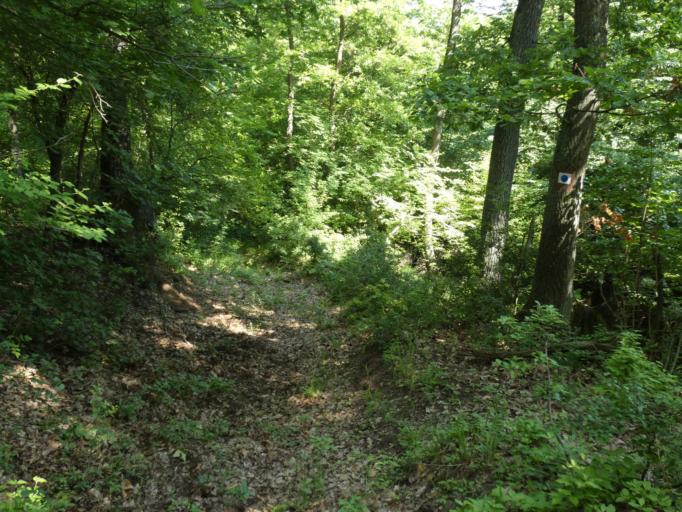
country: HU
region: Pest
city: Szob
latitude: 47.8545
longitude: 18.8442
